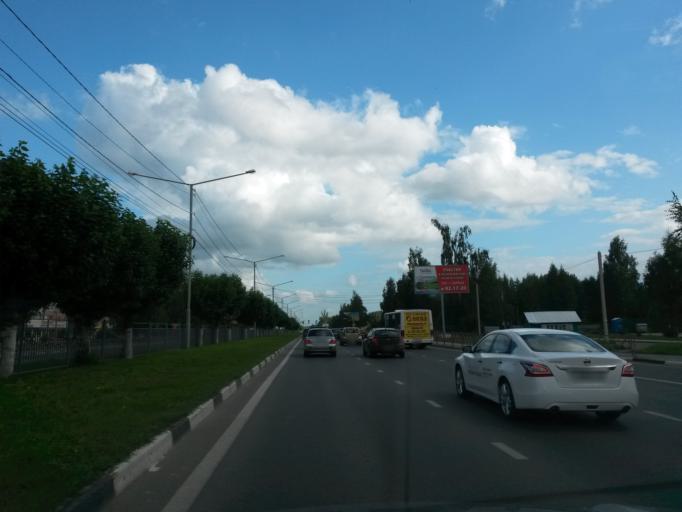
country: RU
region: Jaroslavl
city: Yaroslavl
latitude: 57.5834
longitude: 39.9084
